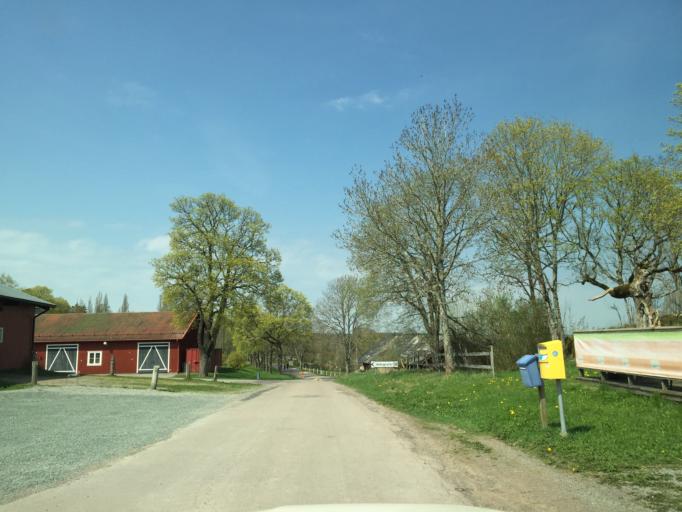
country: SE
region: Vaestra Goetaland
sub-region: Bengtsfors Kommun
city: Billingsfors
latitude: 58.9329
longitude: 12.2104
